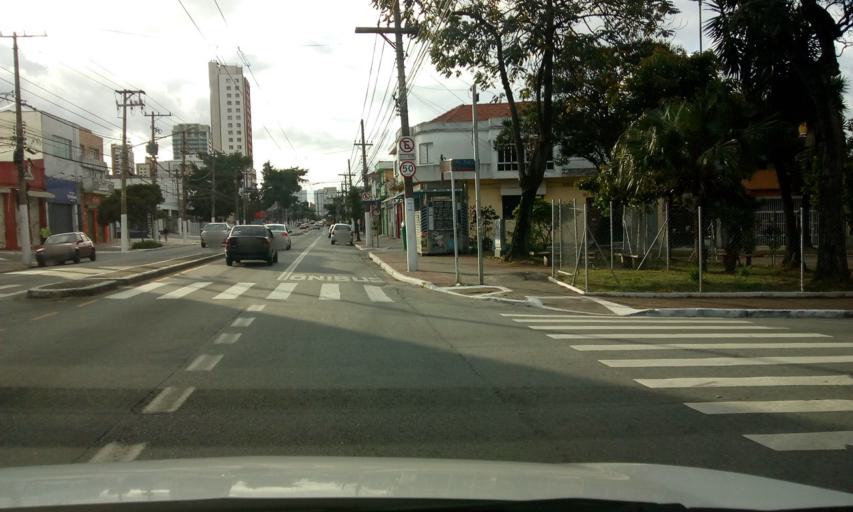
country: BR
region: Sao Paulo
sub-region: Sao Caetano Do Sul
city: Sao Caetano do Sul
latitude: -23.5514
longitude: -46.5312
